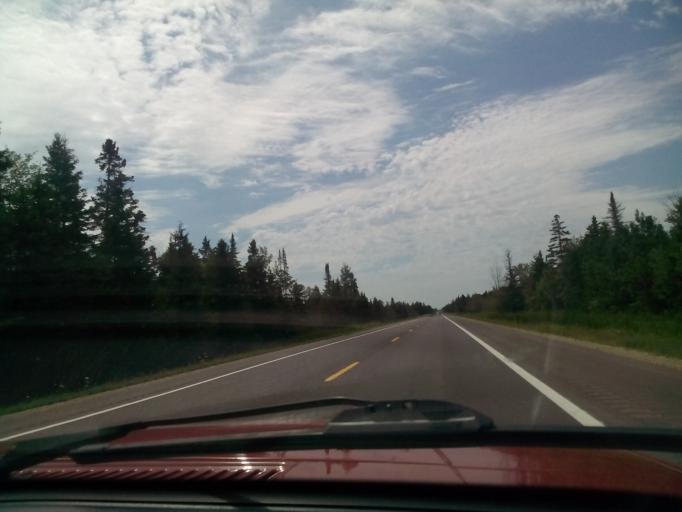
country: US
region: Michigan
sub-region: Schoolcraft County
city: Manistique
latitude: 46.0387
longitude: -85.9745
